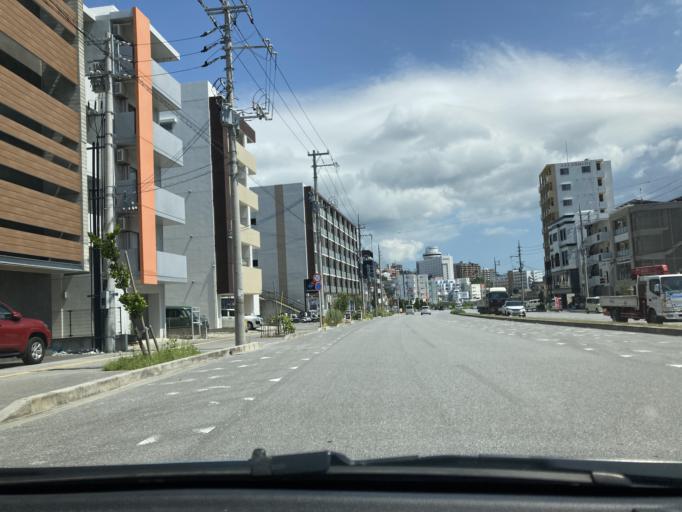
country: JP
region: Okinawa
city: Naha-shi
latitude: 26.2218
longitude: 127.7004
